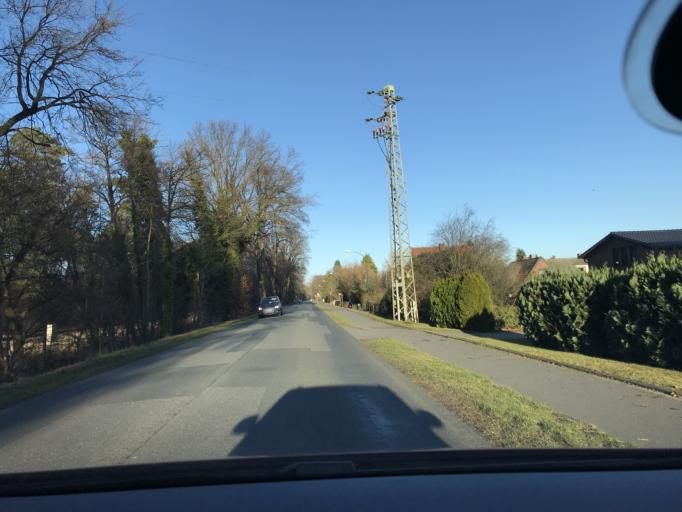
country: DE
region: Lower Saxony
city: Gifhorn
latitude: 52.5033
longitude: 10.5745
